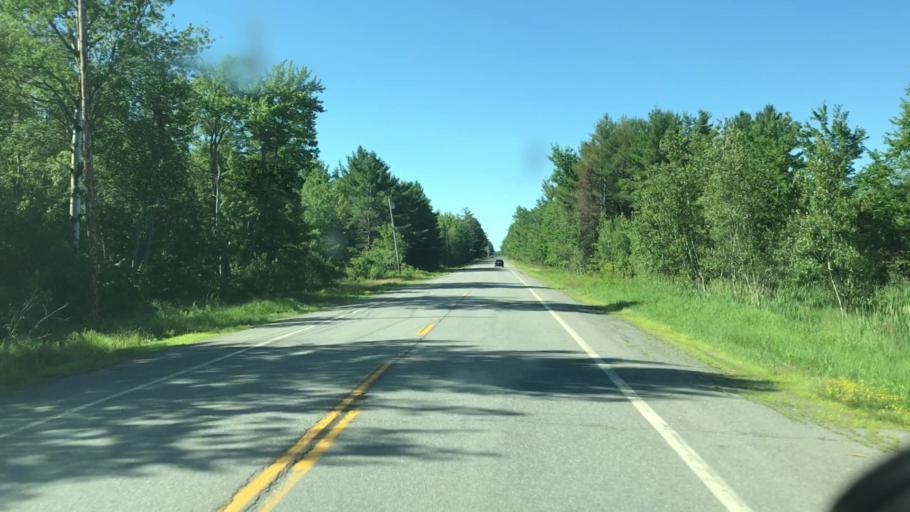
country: US
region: Maine
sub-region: Penobscot County
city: Howland
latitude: 45.2482
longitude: -68.6390
